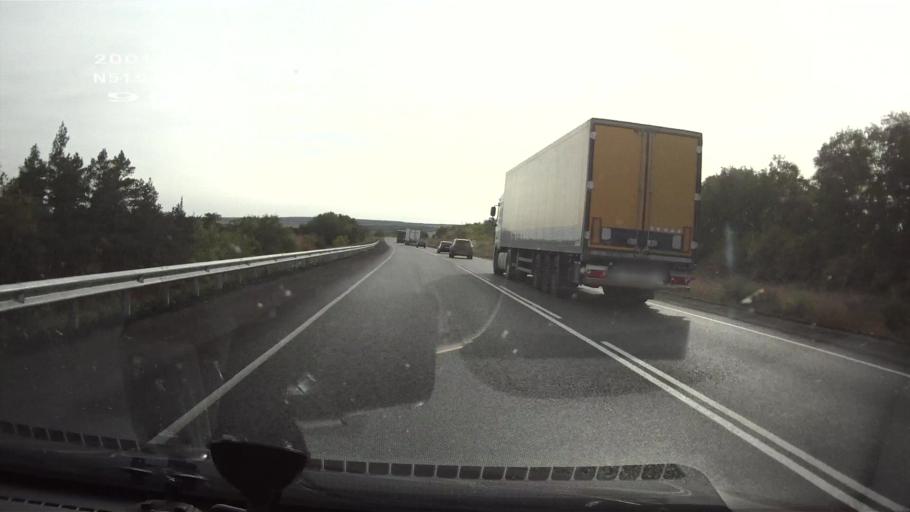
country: RU
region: Saratov
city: Sinodskoye
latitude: 51.9409
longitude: 46.5965
